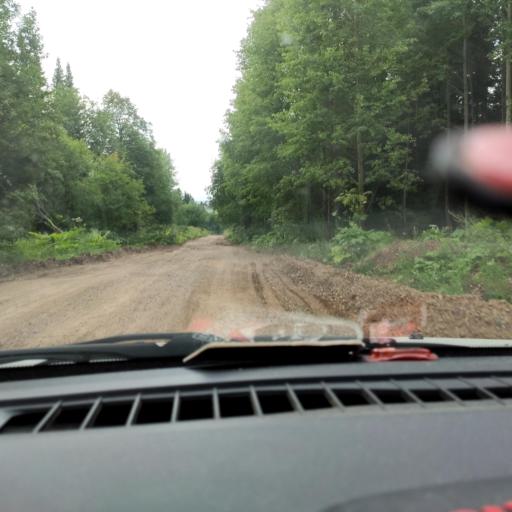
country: RU
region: Perm
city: Kultayevo
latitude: 57.8166
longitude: 56.0006
